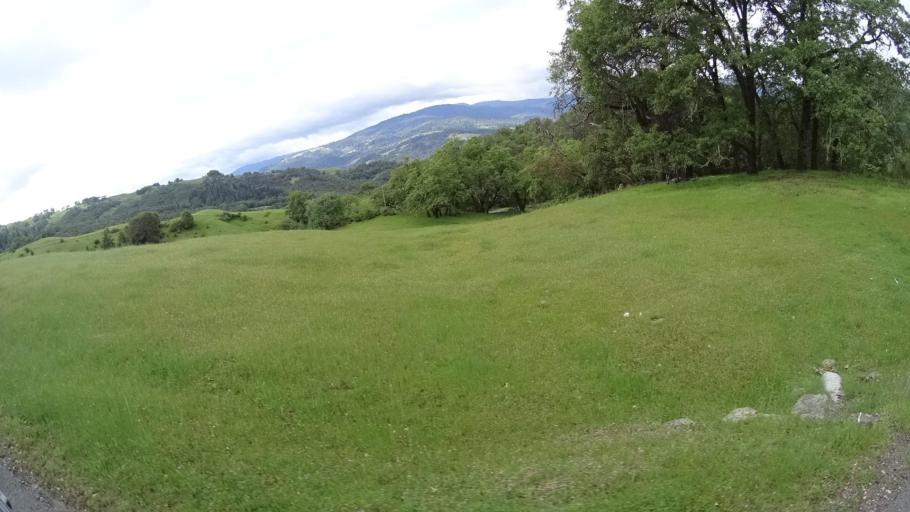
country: US
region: California
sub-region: Humboldt County
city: Redway
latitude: 40.1842
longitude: -123.5770
